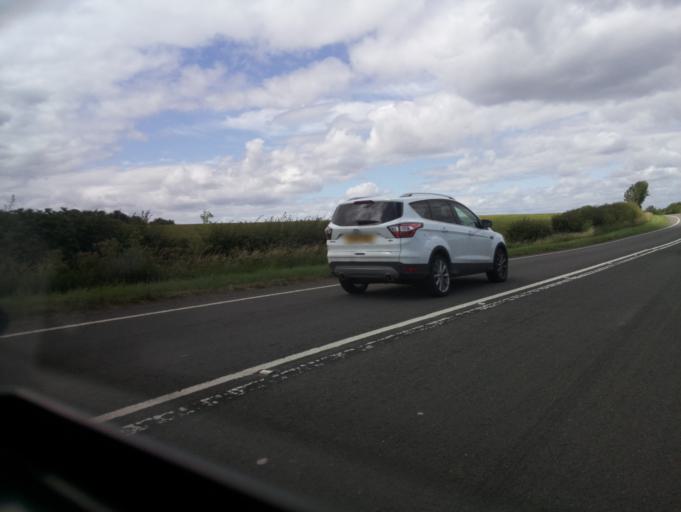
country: GB
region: England
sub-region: Nottinghamshire
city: Cotgrave
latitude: 52.8840
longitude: -1.0684
